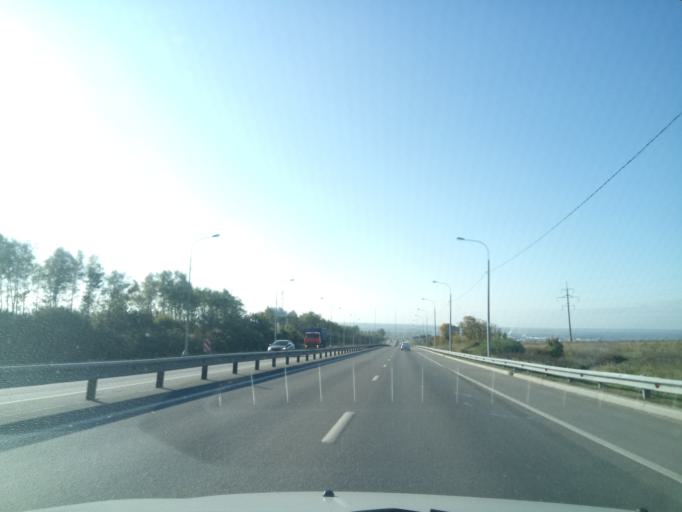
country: RU
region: Nizjnij Novgorod
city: Burevestnik
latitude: 56.2011
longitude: 43.9254
